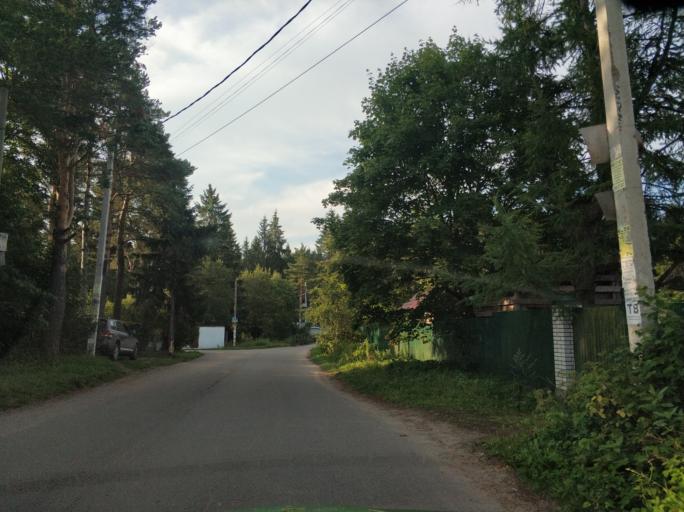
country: RU
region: Leningrad
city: Shcheglovo
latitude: 60.0524
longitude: 30.7451
